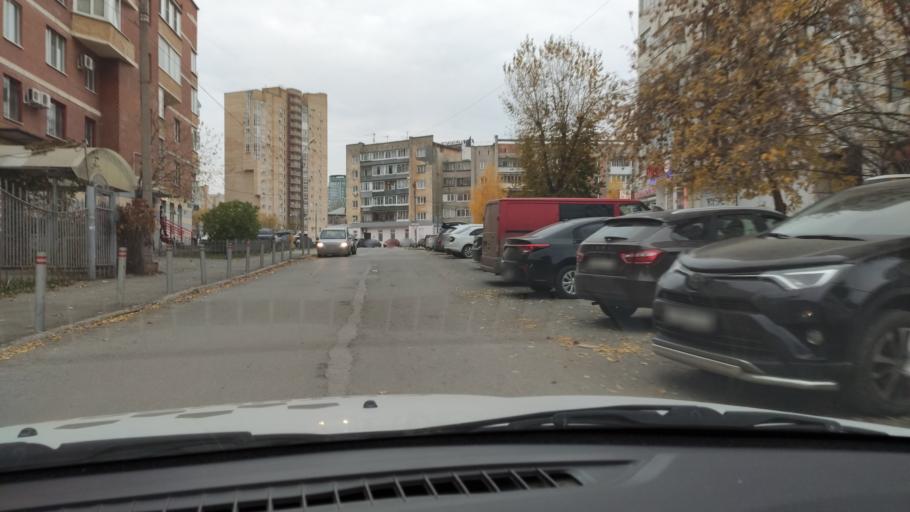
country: RU
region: Perm
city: Perm
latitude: 58.0071
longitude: 56.2710
